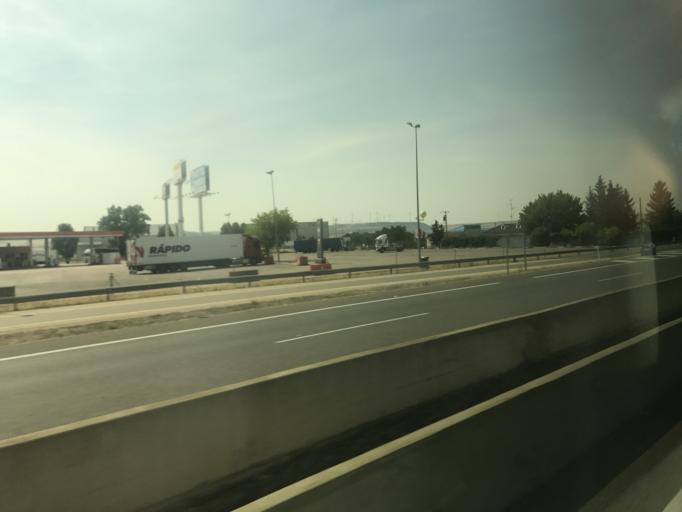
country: ES
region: Castille and Leon
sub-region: Provincia de Palencia
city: Quintana del Puente
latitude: 42.0775
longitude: -4.2117
